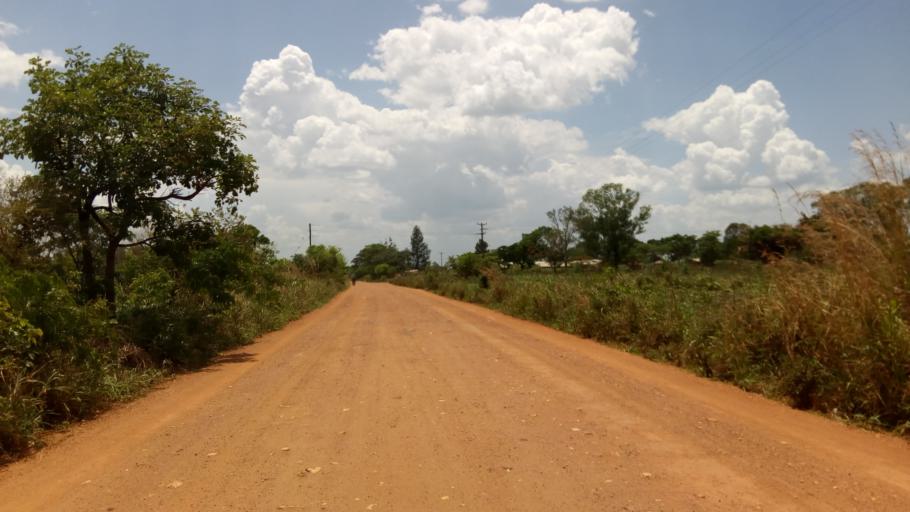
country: UG
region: Northern Region
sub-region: Gulu District
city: Gulu
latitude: 2.7866
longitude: 32.3500
